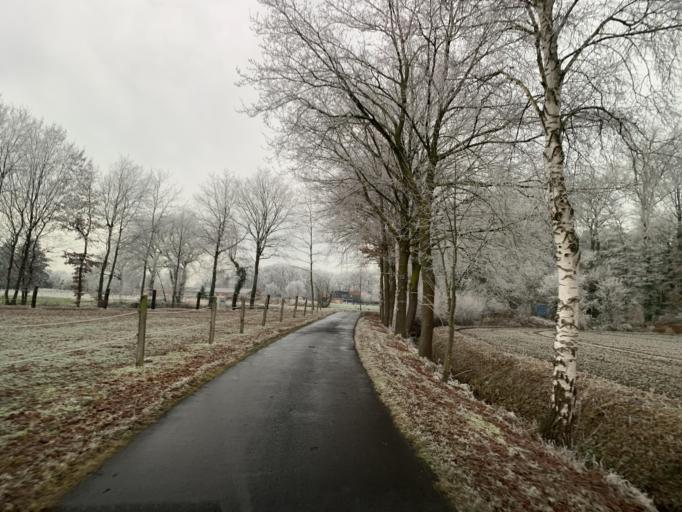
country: DE
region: North Rhine-Westphalia
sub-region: Regierungsbezirk Munster
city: Greven
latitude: 52.0726
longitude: 7.5616
